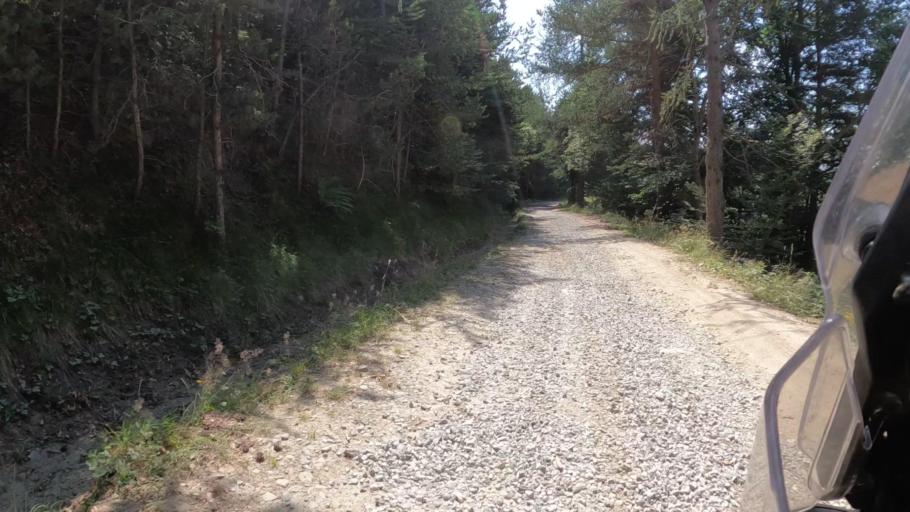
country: IT
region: Piedmont
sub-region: Provincia di Torino
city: Borgone Susa
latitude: 45.1587
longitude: 7.2621
